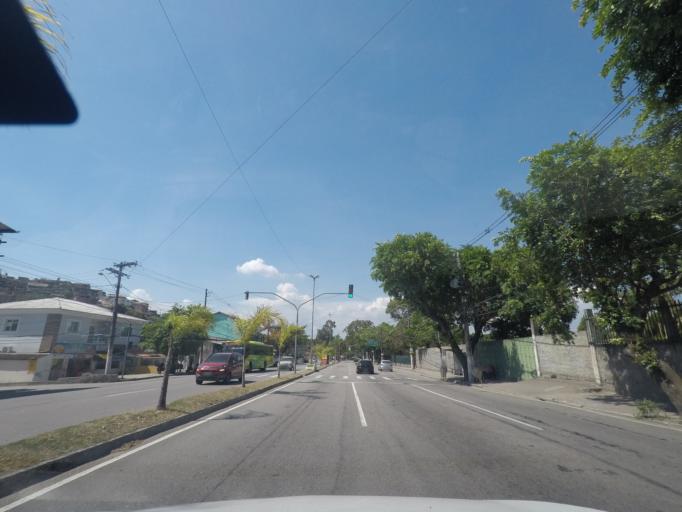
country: BR
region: Rio de Janeiro
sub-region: Niteroi
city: Niteroi
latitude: -22.9141
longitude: -43.0480
